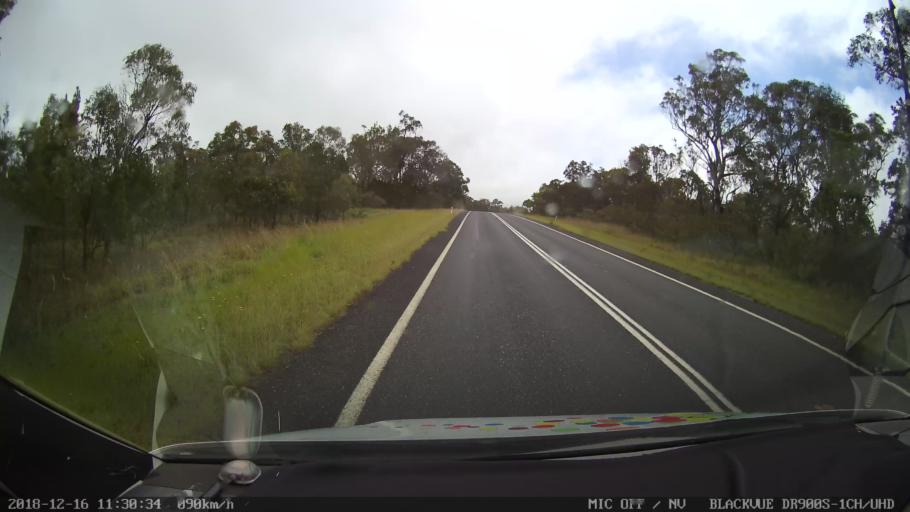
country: AU
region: New South Wales
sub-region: Tenterfield Municipality
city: Carrolls Creek
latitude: -29.0309
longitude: 152.1211
